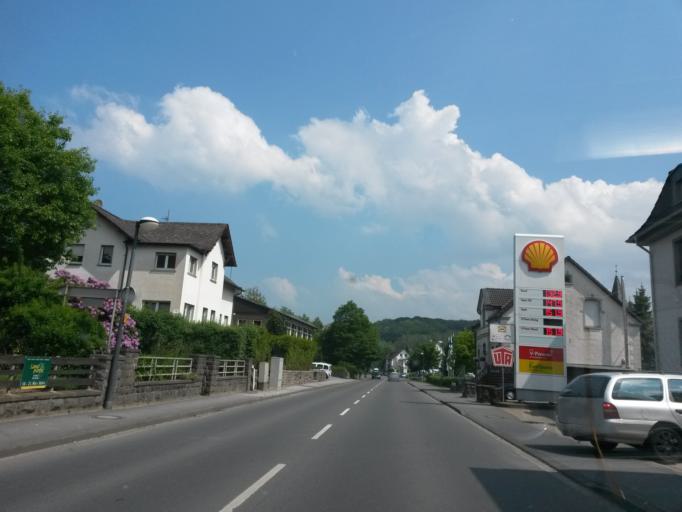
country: DE
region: North Rhine-Westphalia
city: Balve
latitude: 51.3331
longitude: 7.8659
